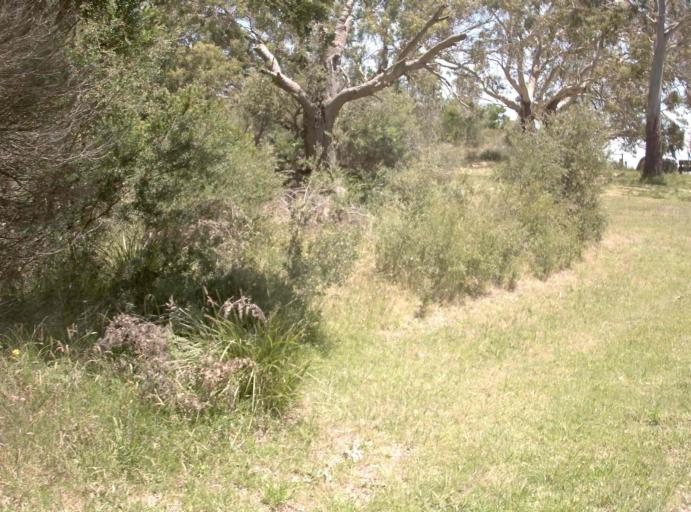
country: AU
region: Victoria
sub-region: Latrobe
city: Morwell
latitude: -38.8560
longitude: 146.2465
